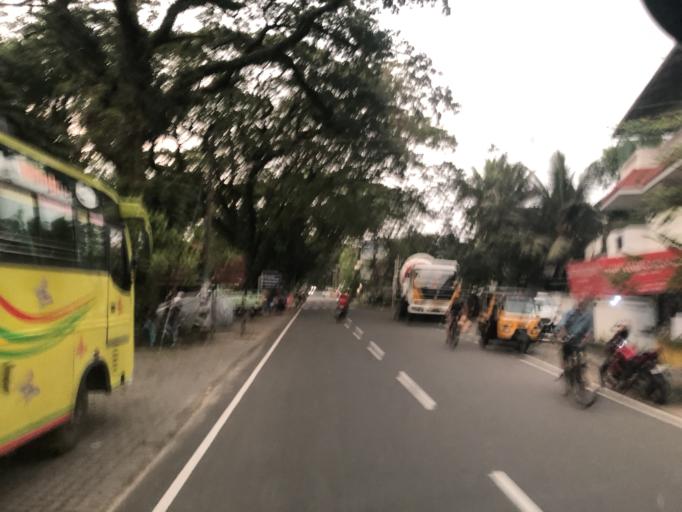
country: IN
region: Kerala
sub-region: Ernakulam
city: Cochin
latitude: 9.9546
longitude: 76.2408
